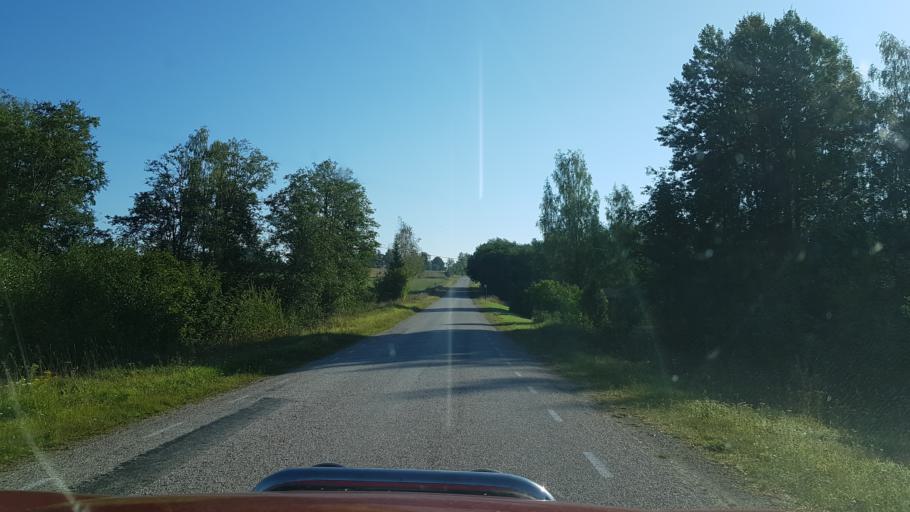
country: EE
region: Jogevamaa
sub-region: Tabivere vald
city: Tabivere
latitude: 58.6749
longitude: 26.7132
